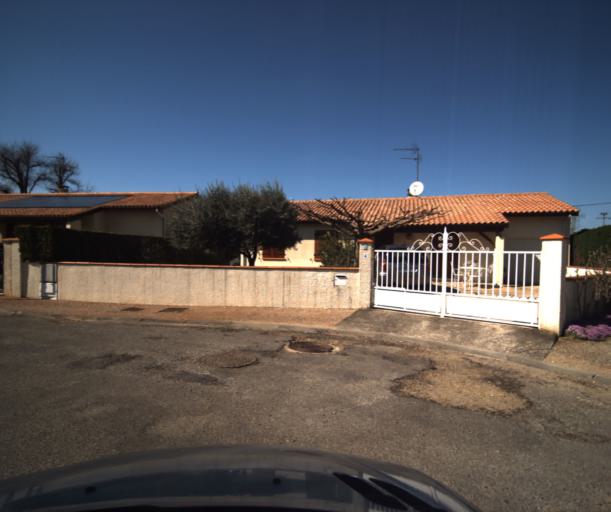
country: FR
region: Midi-Pyrenees
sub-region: Departement du Tarn-et-Garonne
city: Bressols
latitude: 43.9657
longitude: 1.3348
